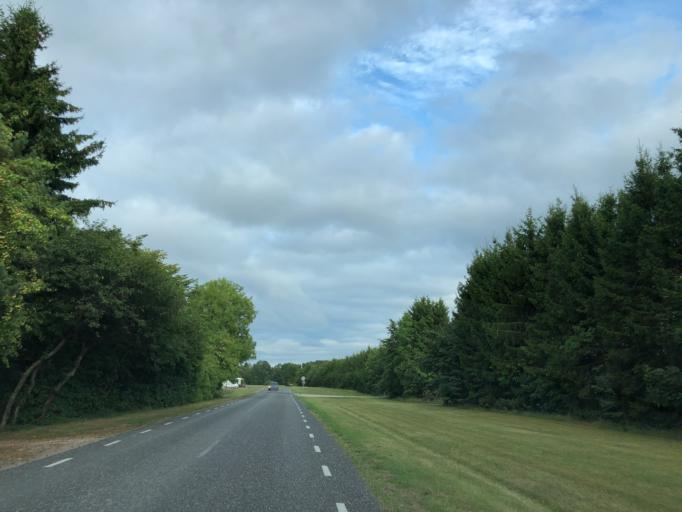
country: EE
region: Hiiumaa
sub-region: Kaerdla linn
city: Kardla
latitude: 58.7895
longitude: 22.8167
